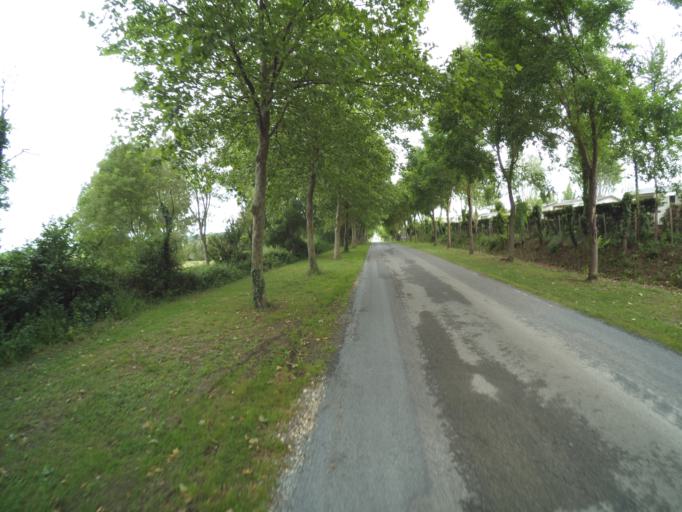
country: FR
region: Poitou-Charentes
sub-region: Departement de la Charente-Maritime
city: Saint-Laurent-de-la-Pree
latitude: 45.9892
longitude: -1.0174
